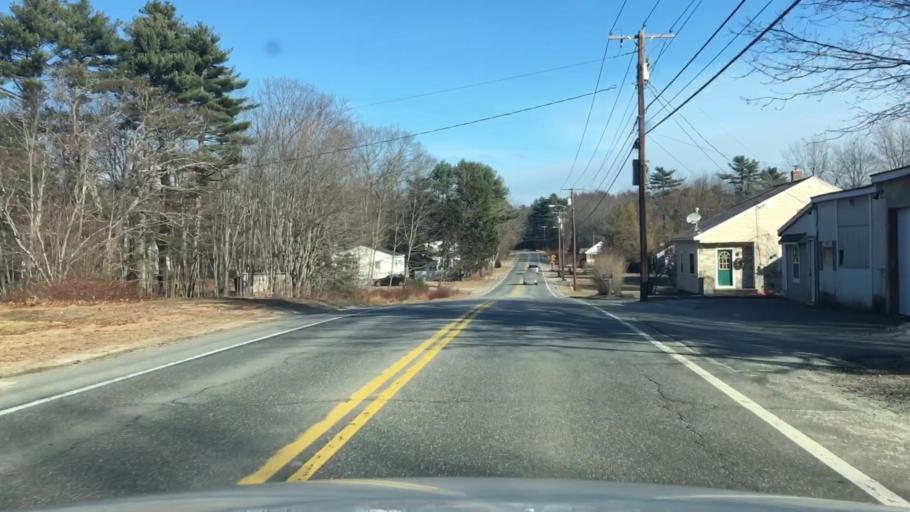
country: US
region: Maine
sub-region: Cumberland County
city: Brunswick
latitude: 43.9394
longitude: -69.9336
